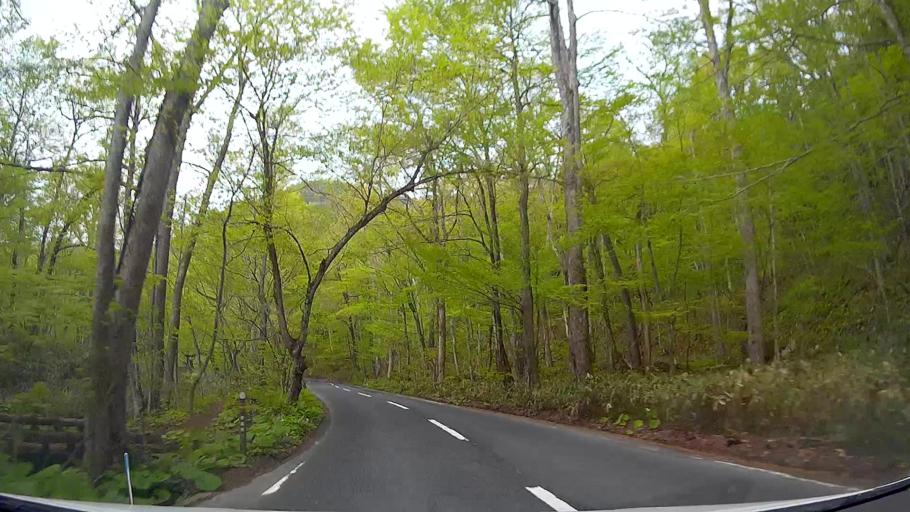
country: JP
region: Aomori
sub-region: Aomori Shi
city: Furudate
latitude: 40.5691
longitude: 140.9784
